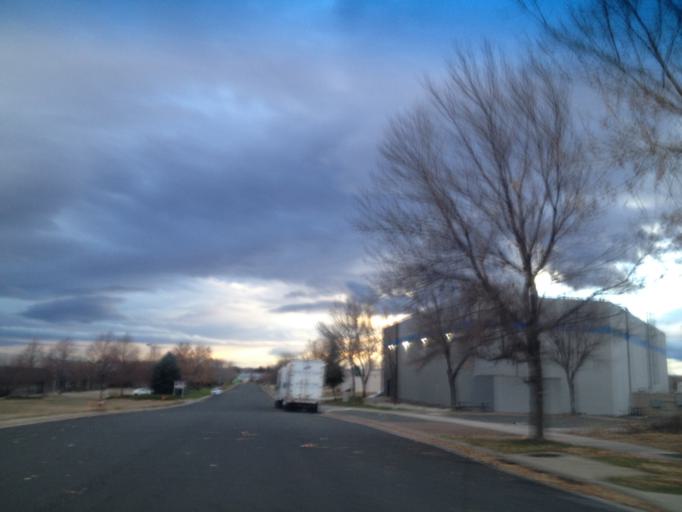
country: US
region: Colorado
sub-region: Boulder County
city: Louisville
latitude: 39.9637
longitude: -105.1243
